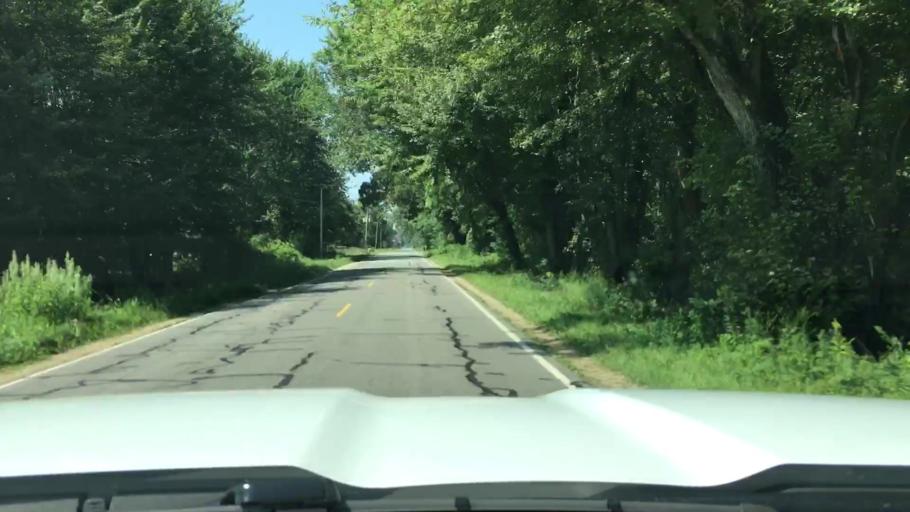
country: US
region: Michigan
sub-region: Saint Joseph County
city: Three Rivers
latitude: 41.9985
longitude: -85.6044
